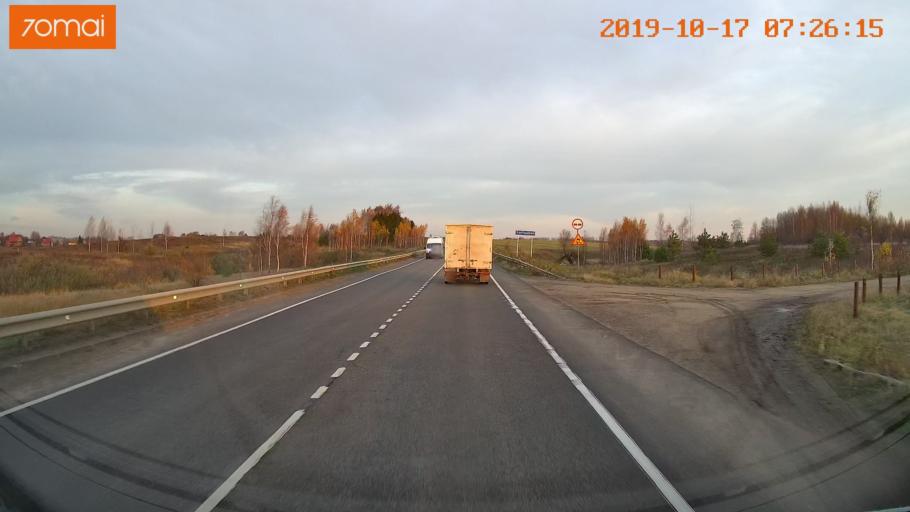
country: RU
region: Ivanovo
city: Gavrilov Posad
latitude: 56.3541
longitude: 40.0963
